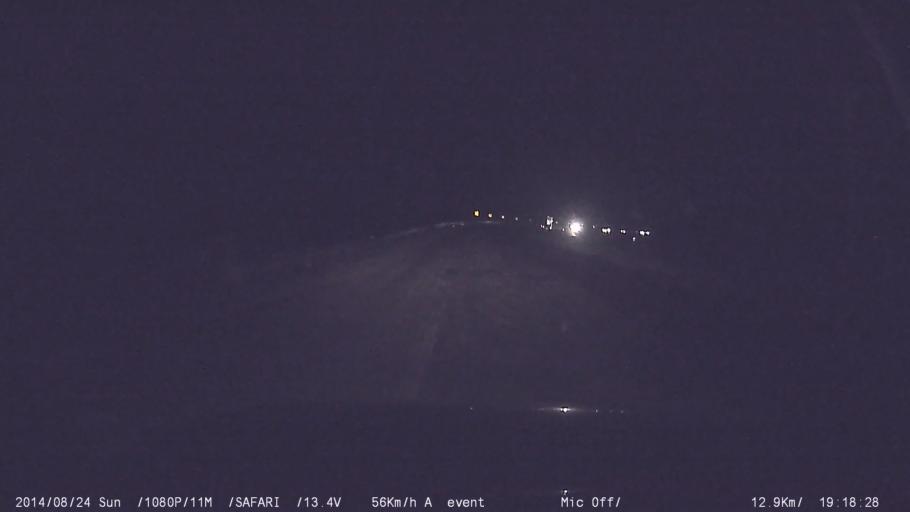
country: IN
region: Tamil Nadu
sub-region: Kancheepuram
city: Kanchipuram
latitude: 12.8741
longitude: 79.6193
